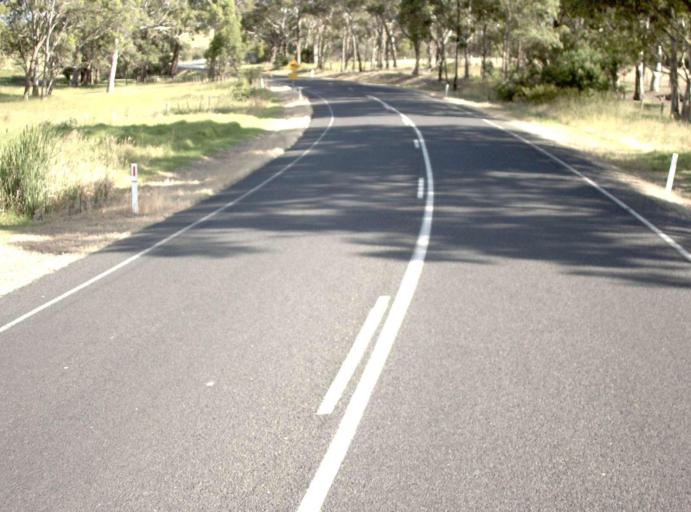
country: AU
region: Victoria
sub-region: East Gippsland
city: Lakes Entrance
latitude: -37.8682
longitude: 147.8483
